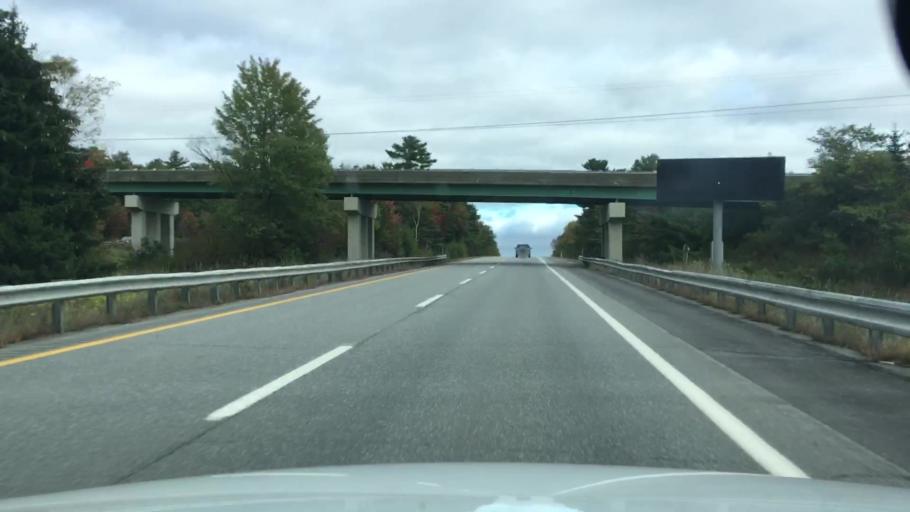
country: US
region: Maine
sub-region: Penobscot County
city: Carmel
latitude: 44.7782
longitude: -69.0626
